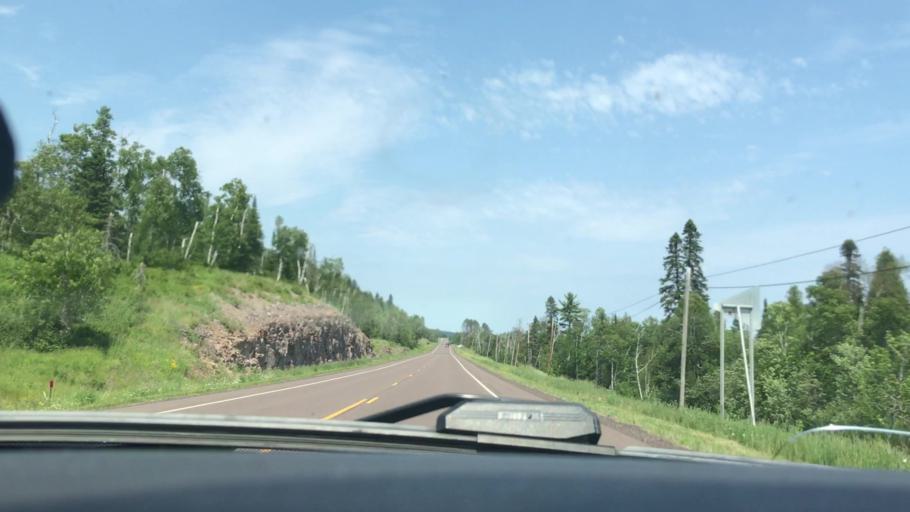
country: US
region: Minnesota
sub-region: Lake County
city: Silver Bay
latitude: 47.4343
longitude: -91.0820
